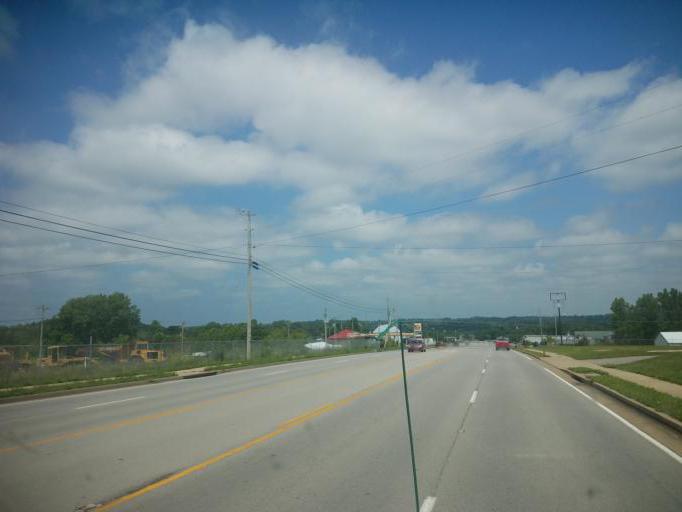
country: US
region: Kentucky
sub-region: Barren County
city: Glasgow
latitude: 36.9792
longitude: -85.8910
